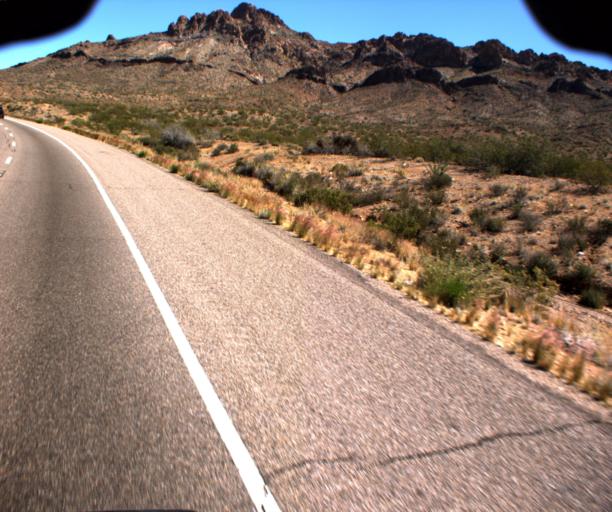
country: US
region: Arizona
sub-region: Mohave County
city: Bullhead City
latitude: 35.1963
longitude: -114.4049
